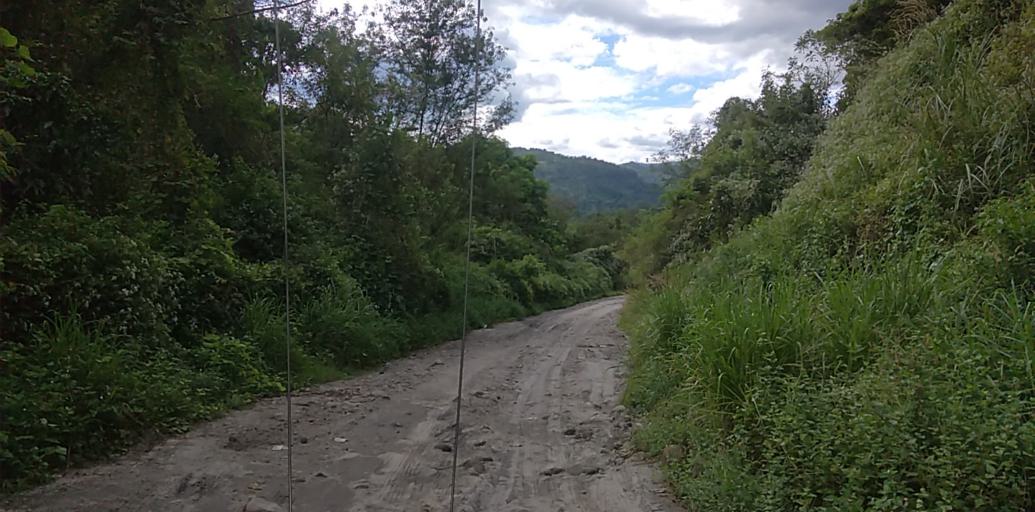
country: PH
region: Central Luzon
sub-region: Province of Pampanga
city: Dolores
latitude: 15.1125
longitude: 120.5032
